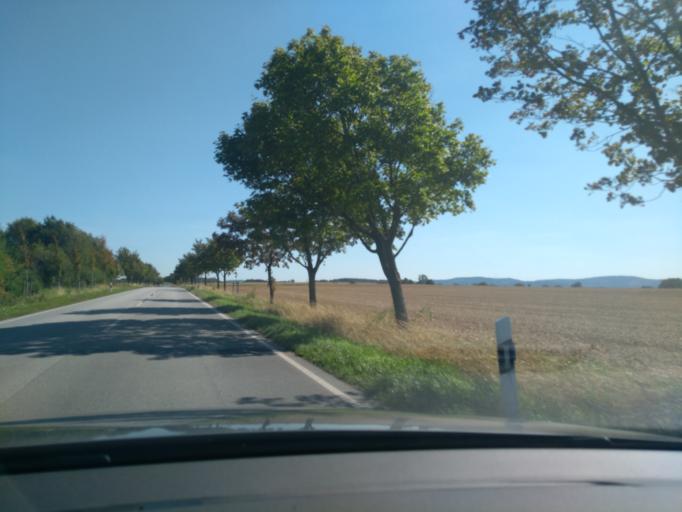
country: DE
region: Saxony
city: Goda
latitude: 51.1991
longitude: 14.3189
